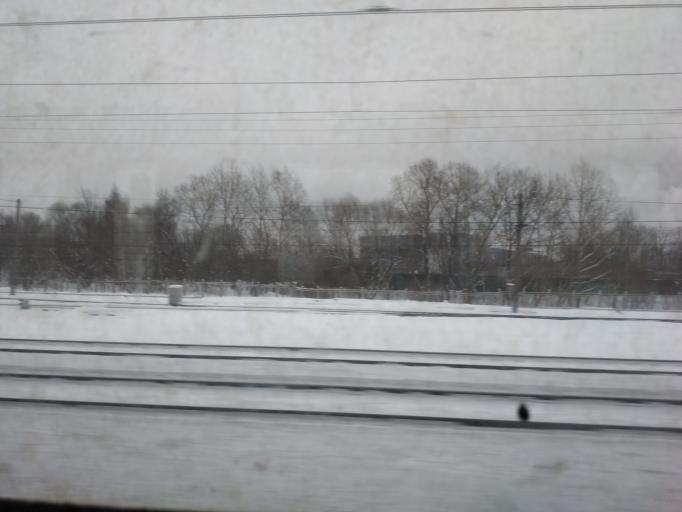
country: RU
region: Moscow
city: Annino
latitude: 55.5859
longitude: 37.6147
